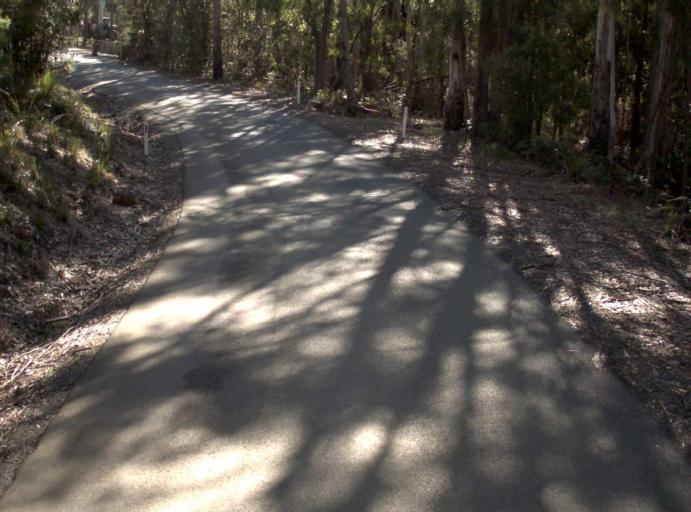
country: AU
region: Tasmania
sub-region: Launceston
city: Mayfield
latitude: -41.3163
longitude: 147.2070
